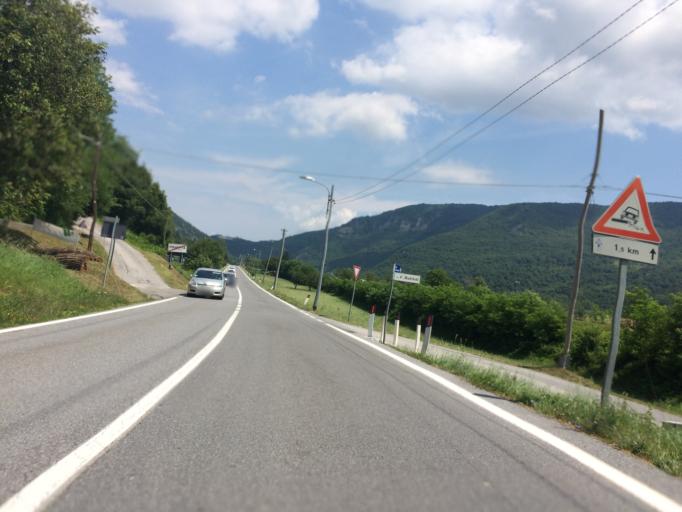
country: IT
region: Piedmont
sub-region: Provincia di Cuneo
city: Priola
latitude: 44.2593
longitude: 8.0234
